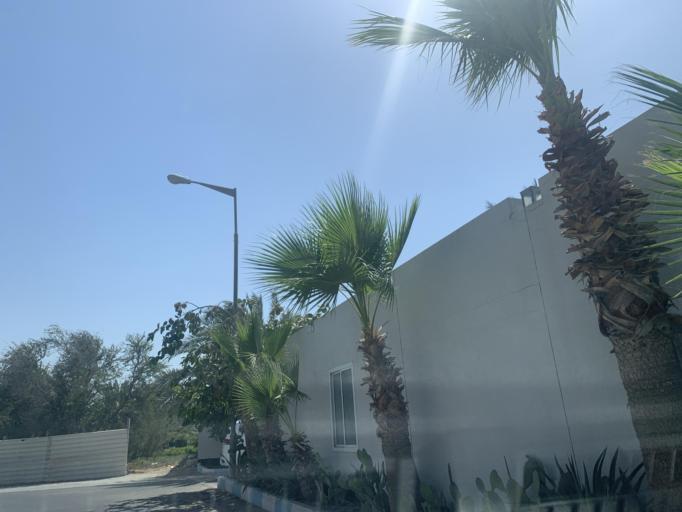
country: BH
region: Manama
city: Jidd Hafs
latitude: 26.2233
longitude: 50.5071
